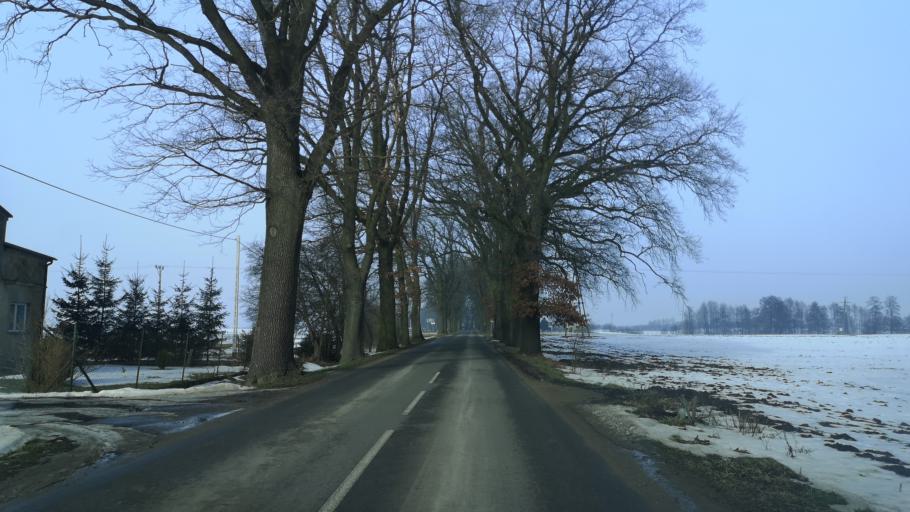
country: PL
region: Warmian-Masurian Voivodeship
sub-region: Powiat nowomiejski
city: Biskupiec
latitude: 53.5052
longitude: 19.3512
